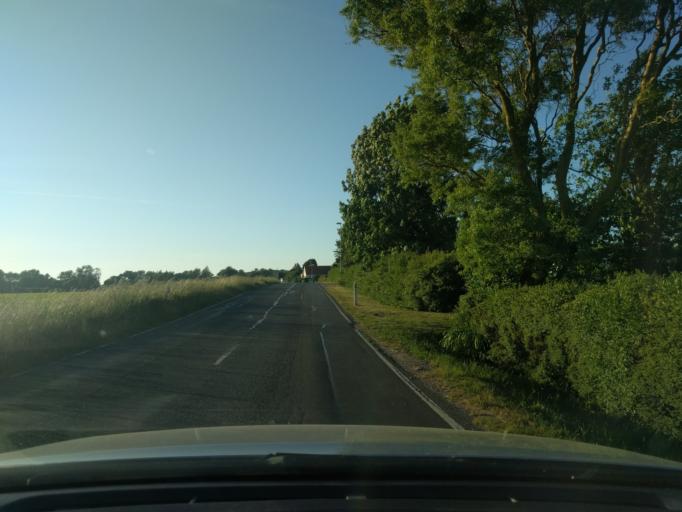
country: DK
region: South Denmark
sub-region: Kerteminde Kommune
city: Kerteminde
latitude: 55.5206
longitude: 10.6550
